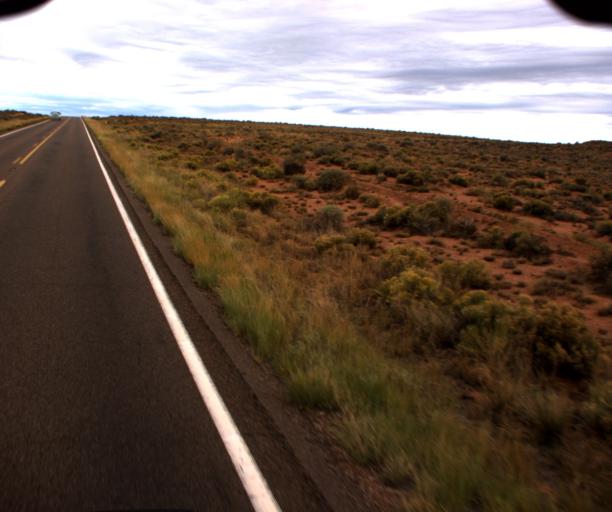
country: US
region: Arizona
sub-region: Navajo County
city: Holbrook
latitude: 34.7507
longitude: -110.1221
